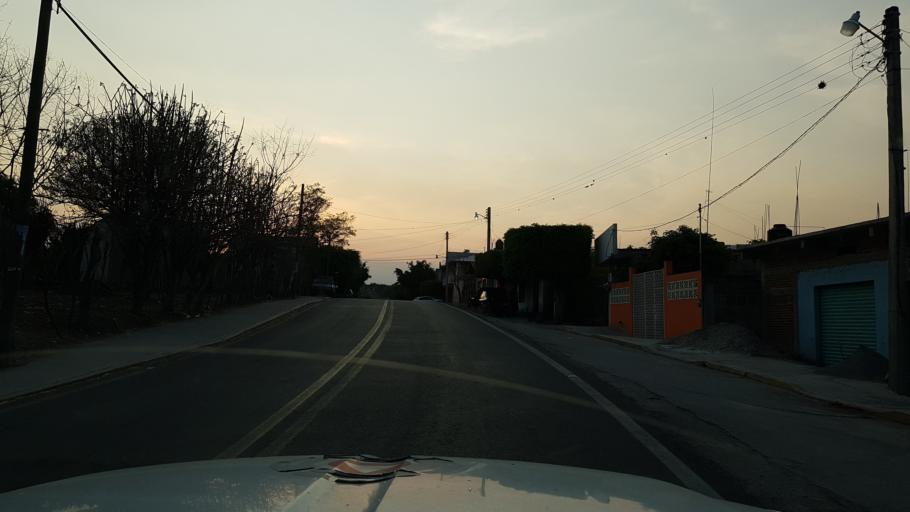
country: MX
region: Morelos
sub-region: Ayala
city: Abelardo L. Rodriguez
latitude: 18.7250
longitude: -98.9964
